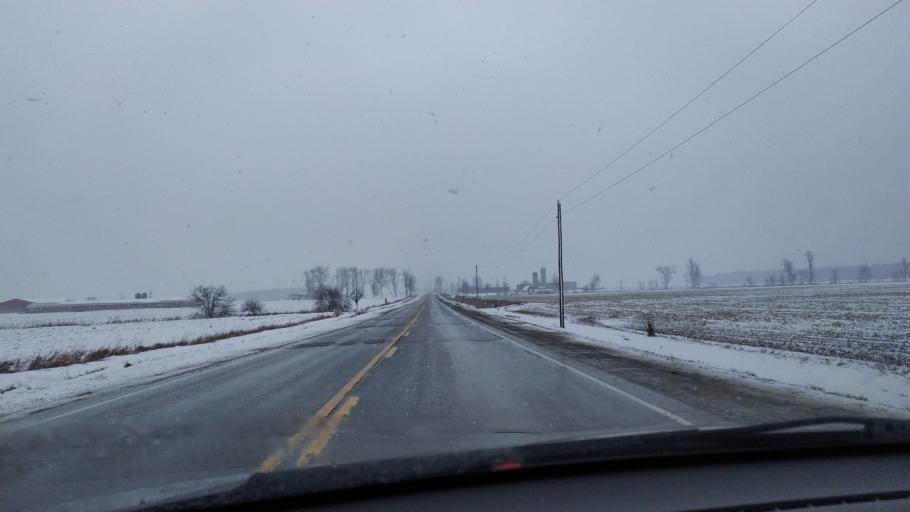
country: CA
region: Ontario
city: Stratford
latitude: 43.5088
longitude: -80.8881
